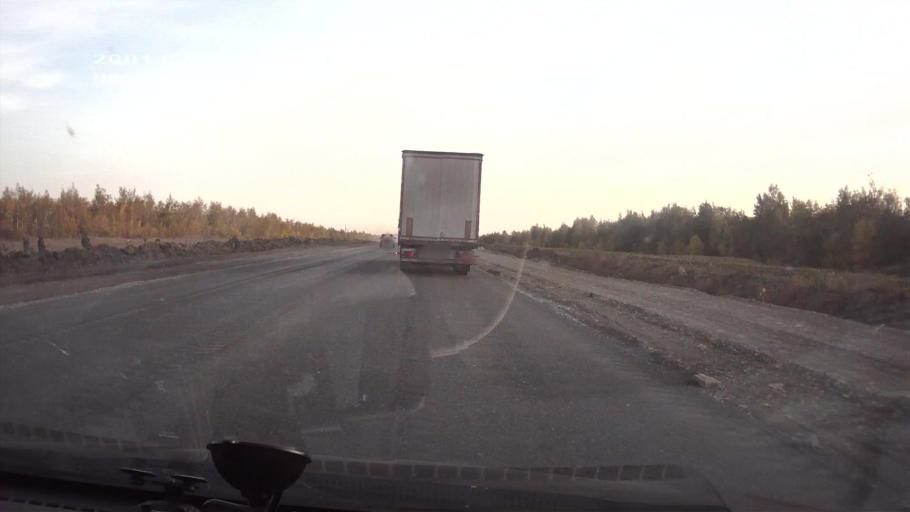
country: RU
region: Saratov
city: Kamenskiy
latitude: 50.9311
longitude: 45.6000
